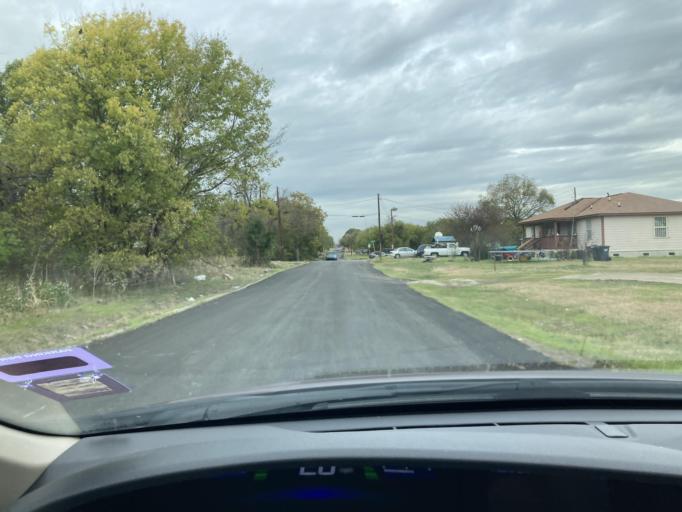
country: US
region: Texas
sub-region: Navarro County
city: Corsicana
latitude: 32.0844
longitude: -96.4553
